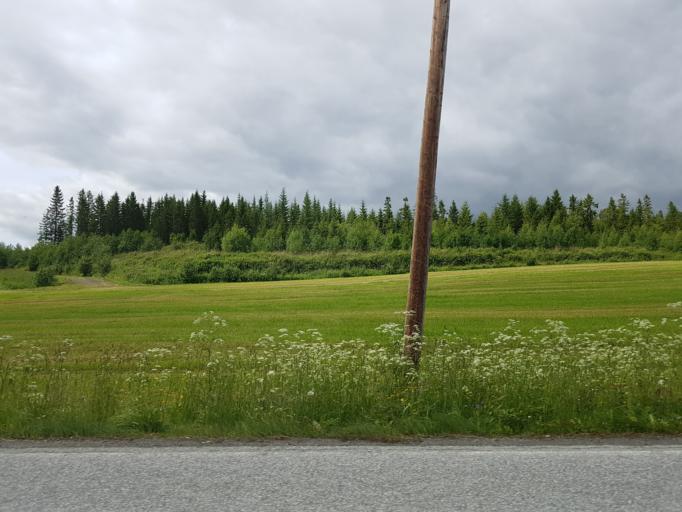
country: NO
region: Sor-Trondelag
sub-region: Selbu
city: Mebonden
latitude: 63.2615
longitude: 11.0815
